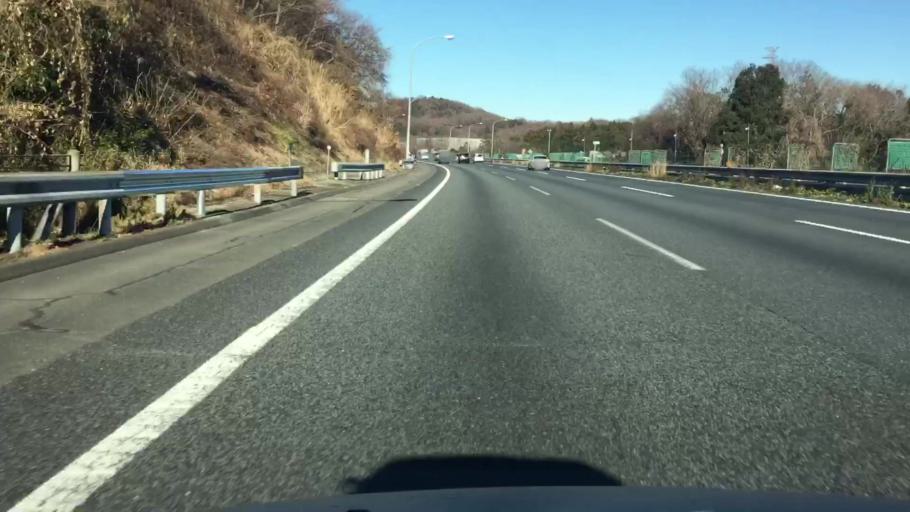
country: JP
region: Saitama
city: Ogawa
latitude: 36.0800
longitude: 139.2989
